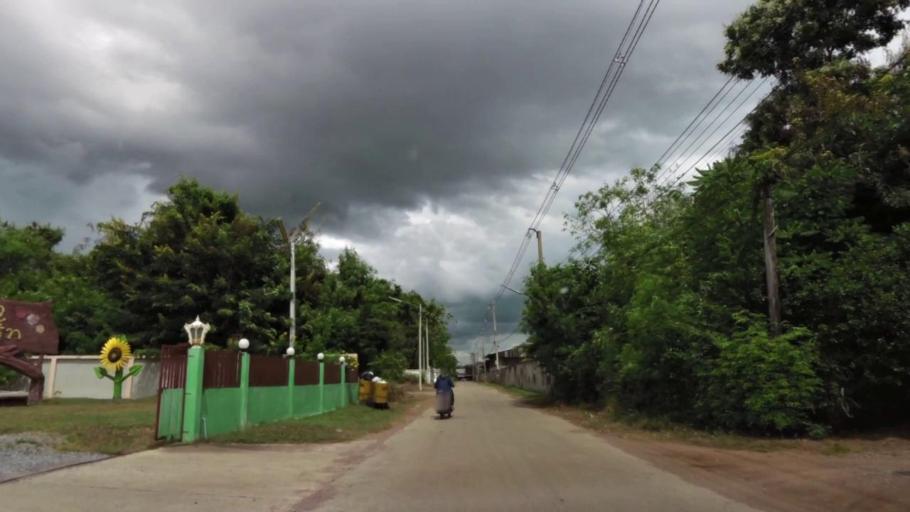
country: TH
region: Nakhon Sawan
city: Phai Sali
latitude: 15.5962
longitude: 100.6493
